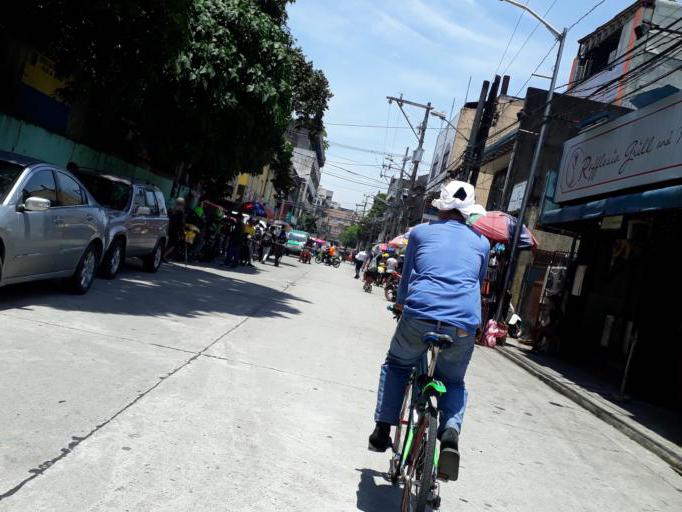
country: PH
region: Metro Manila
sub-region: Caloocan City
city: Niugan
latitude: 14.6507
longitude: 120.9848
